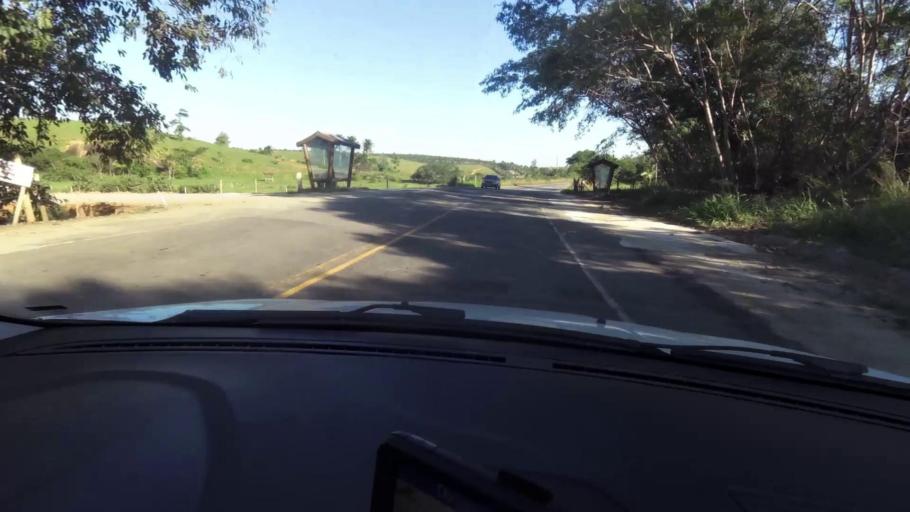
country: BR
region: Espirito Santo
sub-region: Piuma
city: Piuma
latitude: -20.7413
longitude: -40.6476
